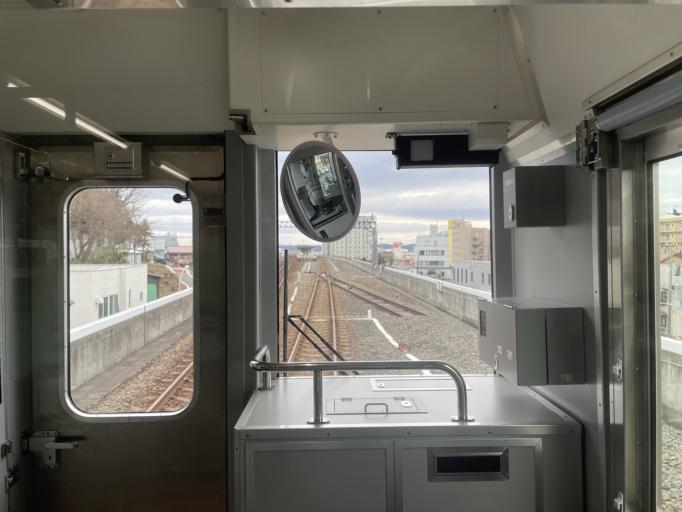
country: JP
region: Aomori
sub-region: Hachinohe Shi
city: Uchimaru
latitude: 40.5160
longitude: 141.4938
